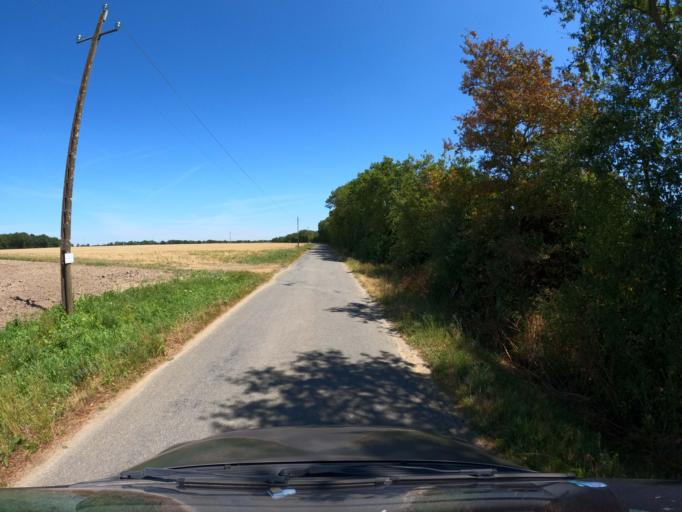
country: FR
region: Pays de la Loire
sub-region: Departement de la Loire-Atlantique
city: La Limouziniere
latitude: 46.9443
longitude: -1.6210
